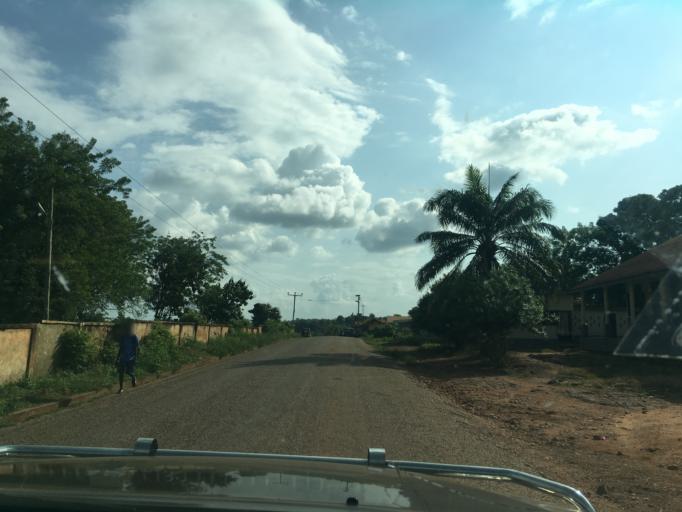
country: GH
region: Western
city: Bibiani
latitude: 6.8026
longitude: -2.5193
